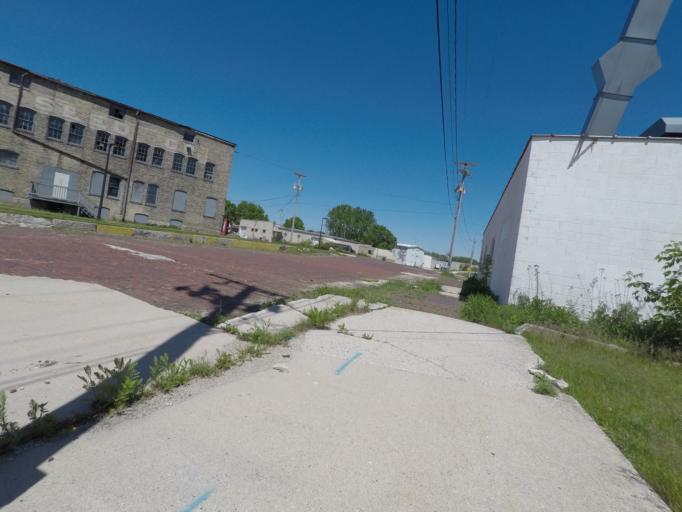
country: US
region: Wisconsin
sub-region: Sheboygan County
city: Sheboygan
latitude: 43.7518
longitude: -87.7200
